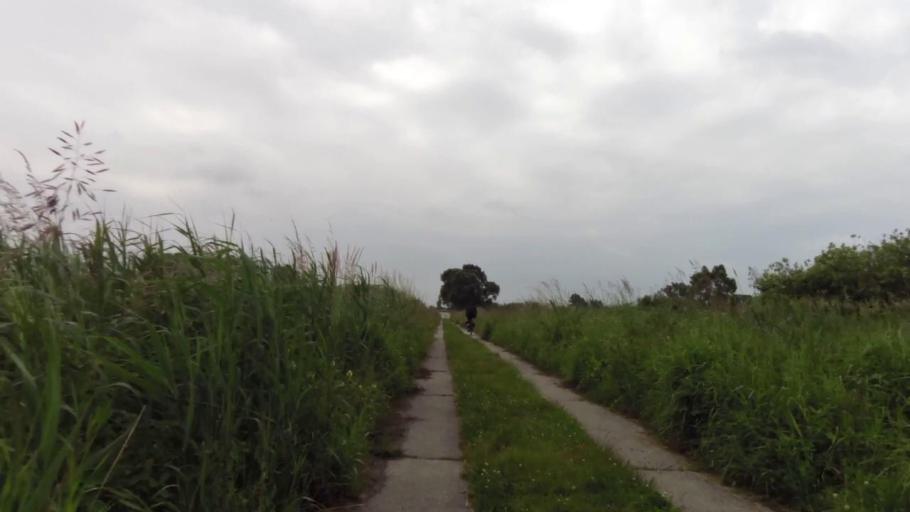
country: PL
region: West Pomeranian Voivodeship
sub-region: Powiat goleniowski
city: Stepnica
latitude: 53.5558
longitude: 14.7018
